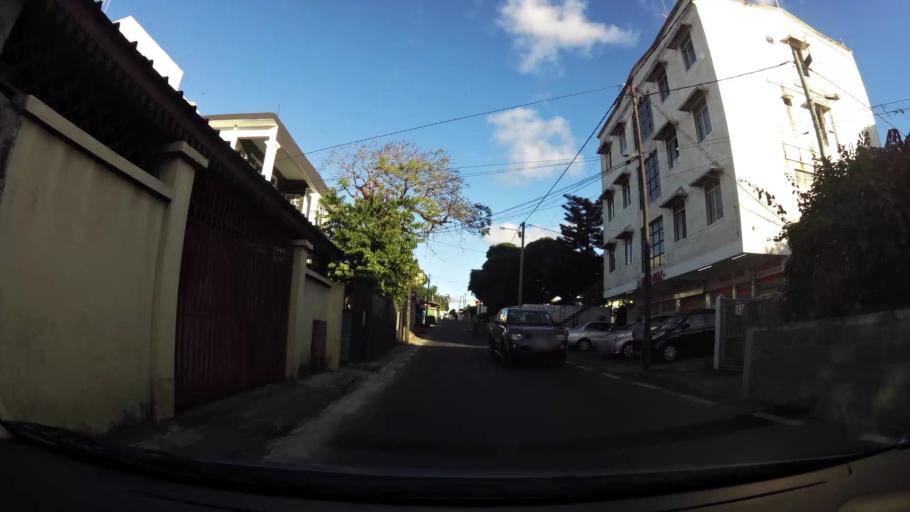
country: MU
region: Plaines Wilhems
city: Quatre Bornes
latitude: -20.2452
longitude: 57.4674
